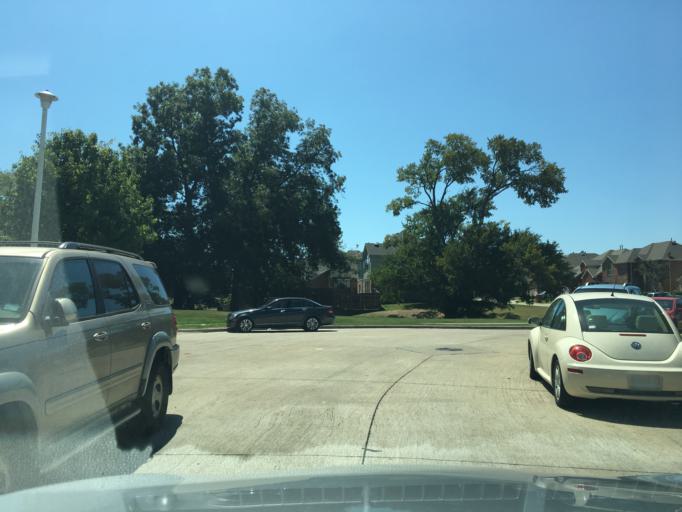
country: US
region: Texas
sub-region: Dallas County
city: Garland
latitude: 32.9514
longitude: -96.6421
